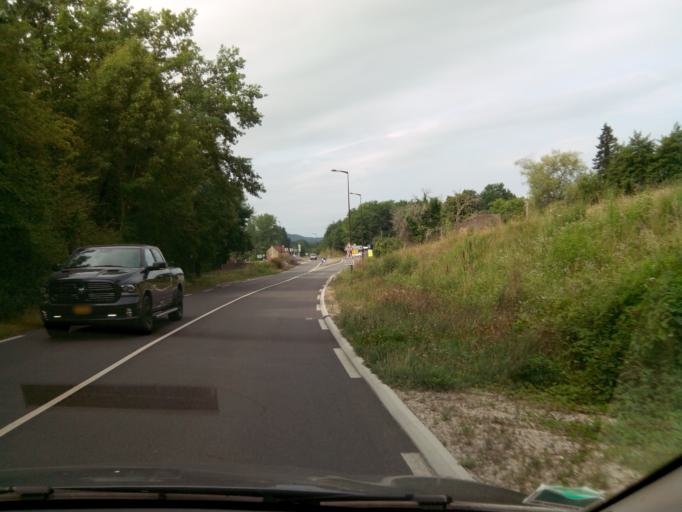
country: FR
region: Aquitaine
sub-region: Departement de la Dordogne
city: Eyvigues-et-Eybenes
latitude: 44.8542
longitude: 1.3374
